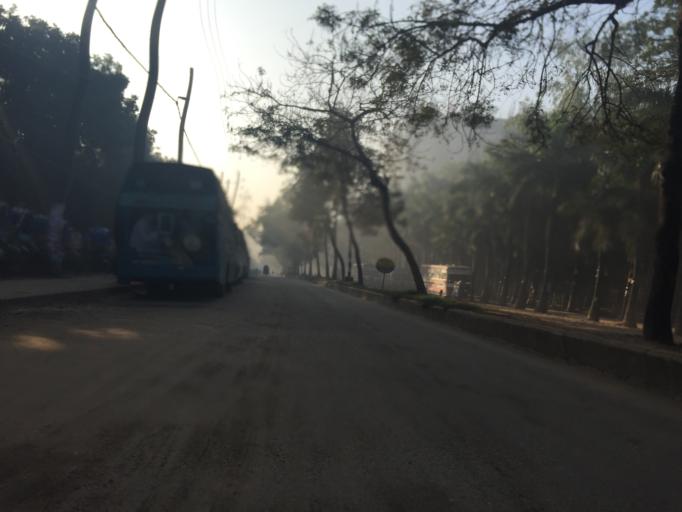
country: BD
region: Dhaka
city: Azimpur
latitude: 23.8097
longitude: 90.3501
